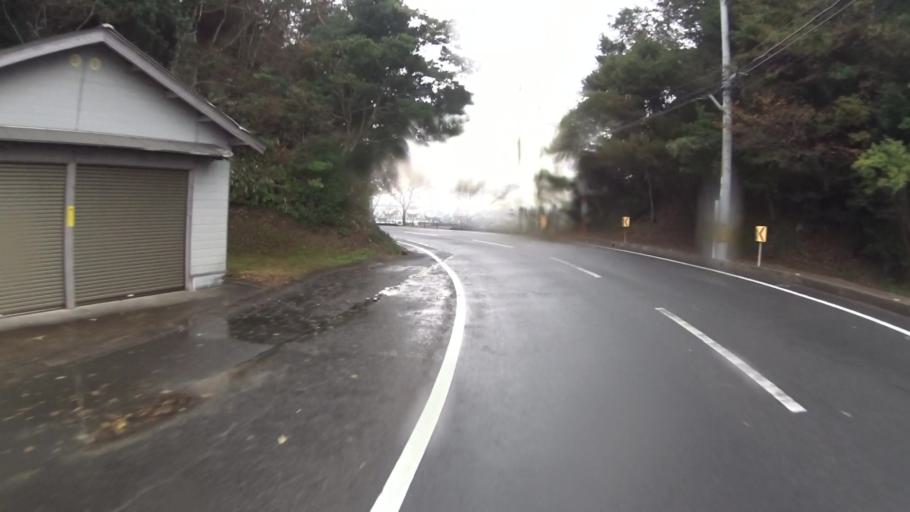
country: JP
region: Kyoto
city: Miyazu
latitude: 35.5835
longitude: 135.2304
